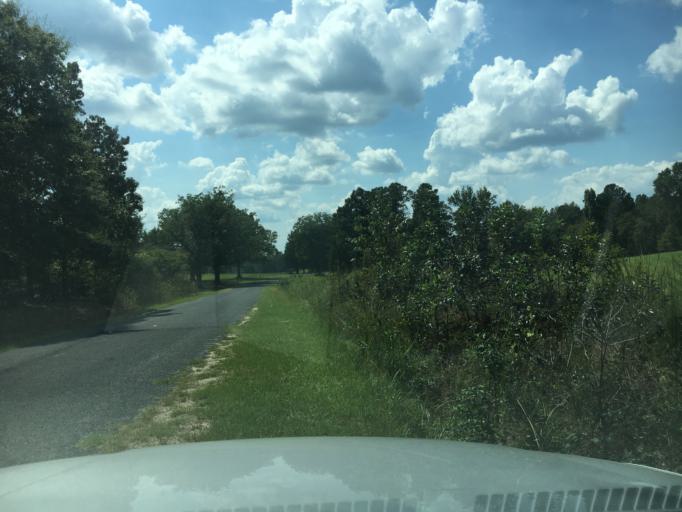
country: US
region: South Carolina
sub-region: Greenwood County
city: Greenwood
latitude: 34.0610
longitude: -82.1540
